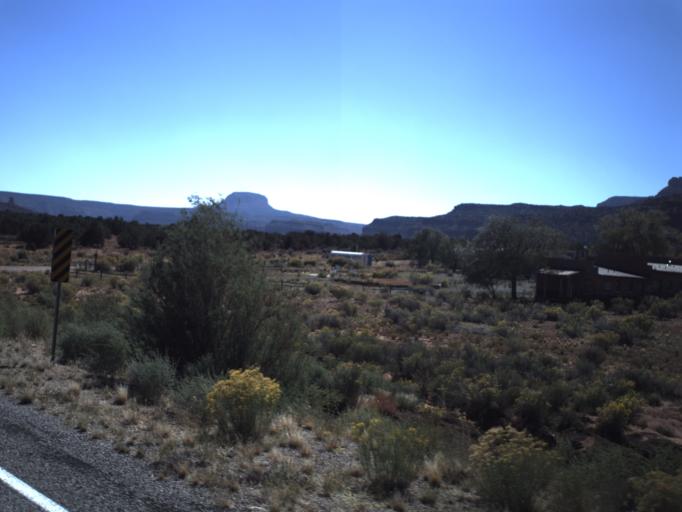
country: US
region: Utah
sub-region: San Juan County
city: Blanding
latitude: 37.6360
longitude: -110.1571
